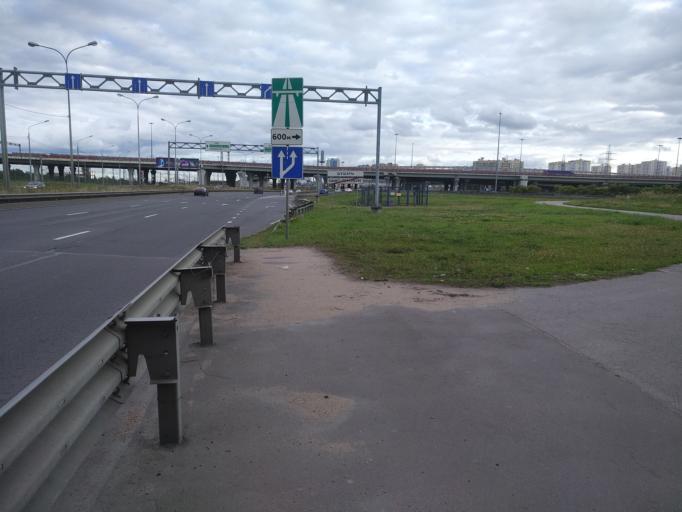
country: RU
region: St.-Petersburg
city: Shushary
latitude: 59.8187
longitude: 30.3805
